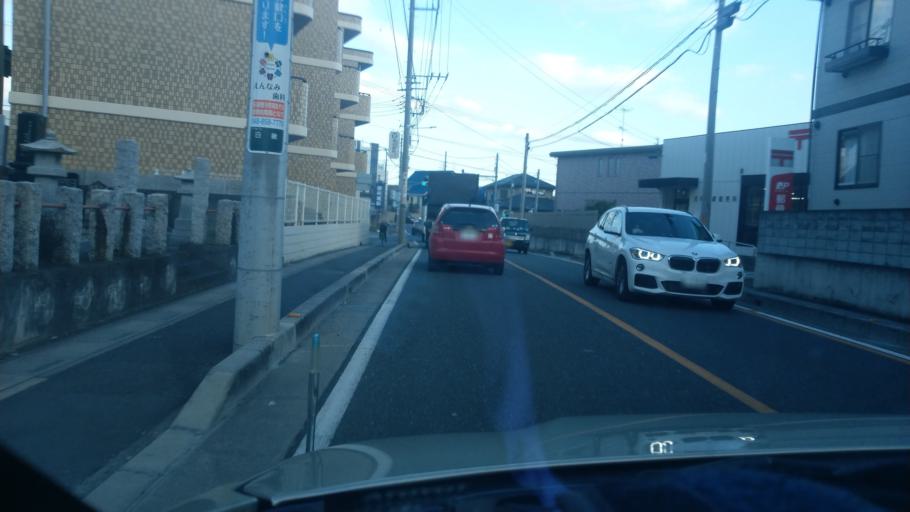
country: JP
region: Saitama
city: Yono
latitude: 35.8823
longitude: 139.6038
